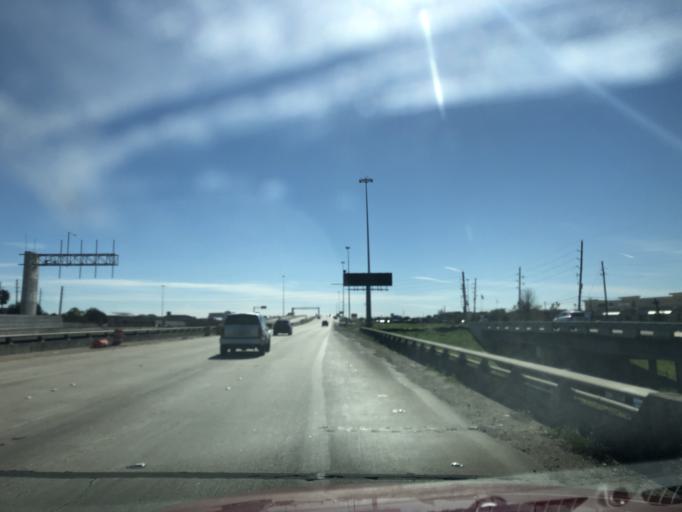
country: US
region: Texas
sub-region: Brazoria County
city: Brookside Village
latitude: 29.5863
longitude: -95.3866
